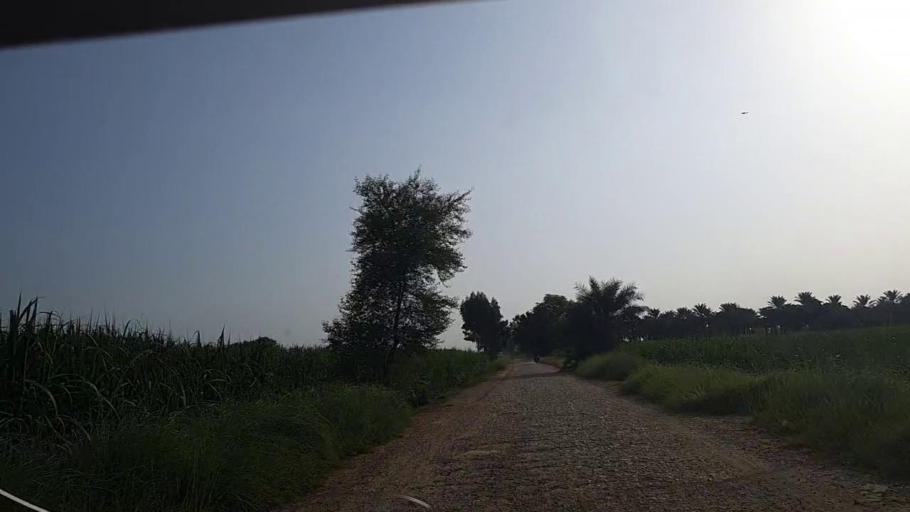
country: PK
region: Sindh
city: Ghotki
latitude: 27.9936
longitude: 69.2661
